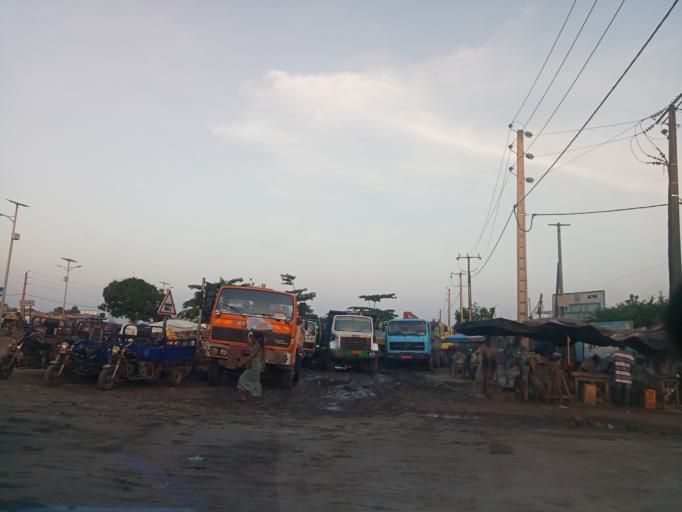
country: BJ
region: Atlantique
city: Hevie
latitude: 6.3863
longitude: 2.2871
